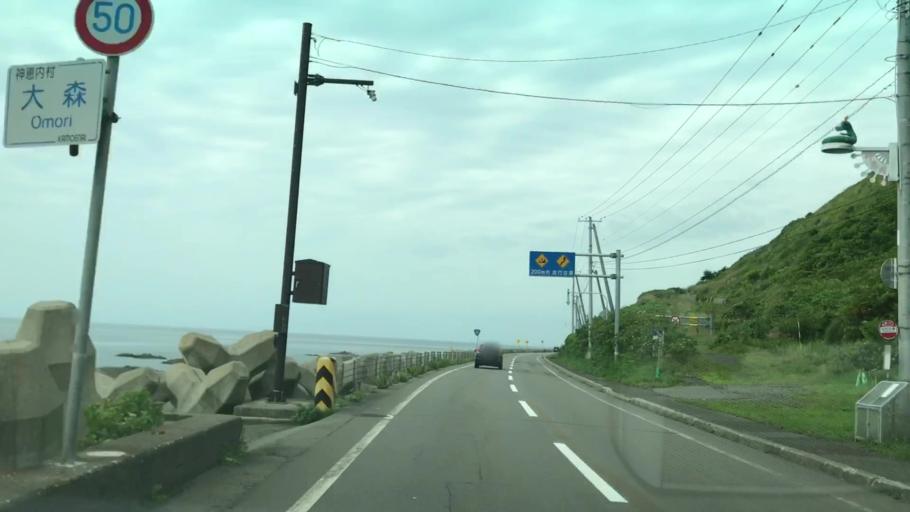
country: JP
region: Hokkaido
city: Iwanai
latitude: 43.1622
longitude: 140.3913
